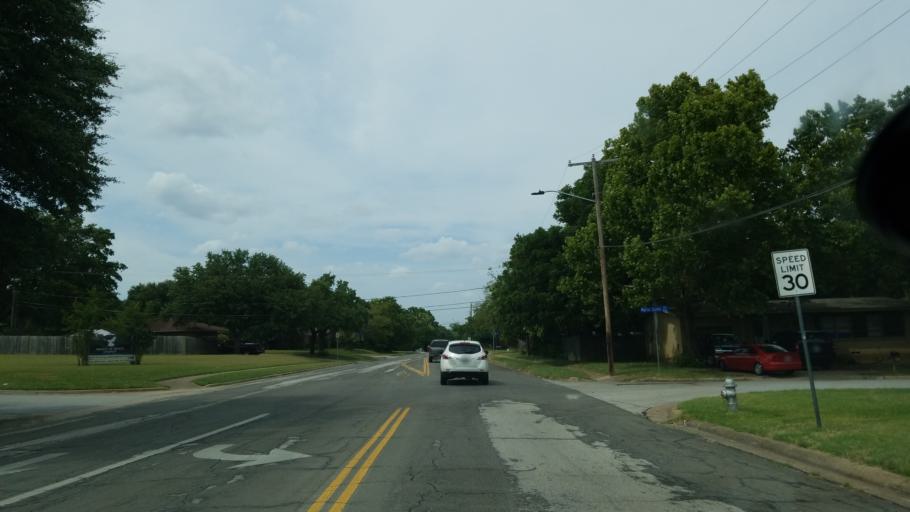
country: US
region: Texas
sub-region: Tarrant County
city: Arlington
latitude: 32.7216
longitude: -97.0833
